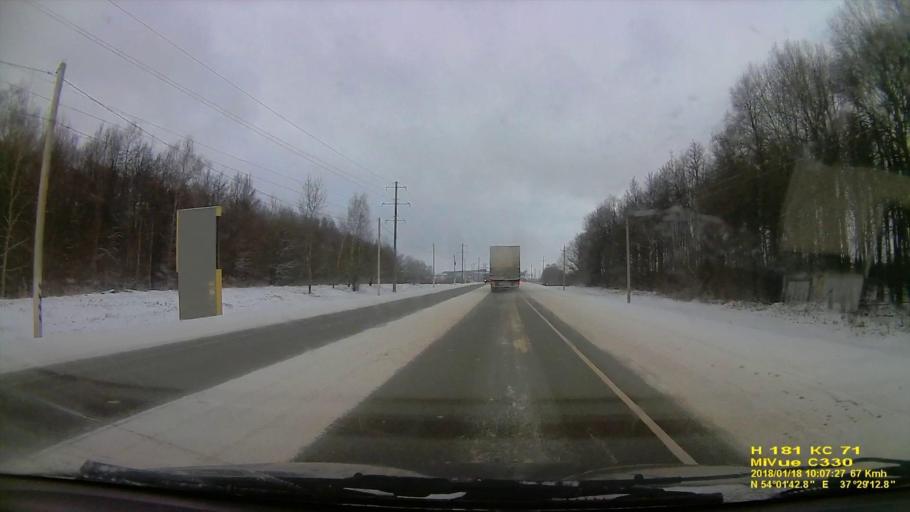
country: RU
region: Tula
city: Pervomayskiy
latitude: 54.0284
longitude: 37.4869
